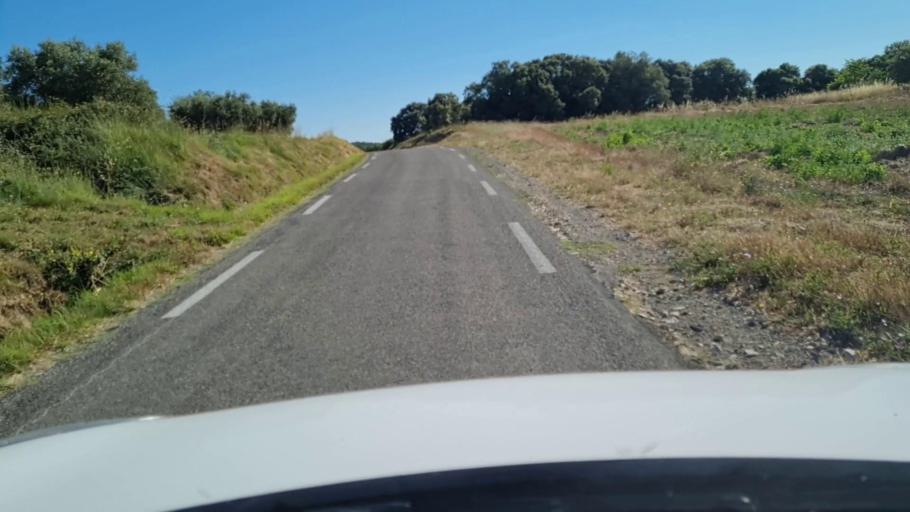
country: FR
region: Languedoc-Roussillon
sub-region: Departement du Gard
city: Sommieres
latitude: 43.7975
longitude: 4.0365
